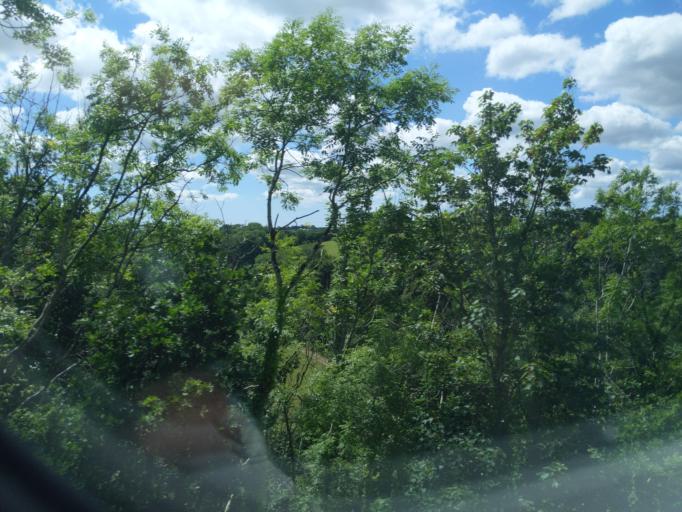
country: GB
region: England
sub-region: Cornwall
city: Liskeard
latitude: 50.4395
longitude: -4.4523
